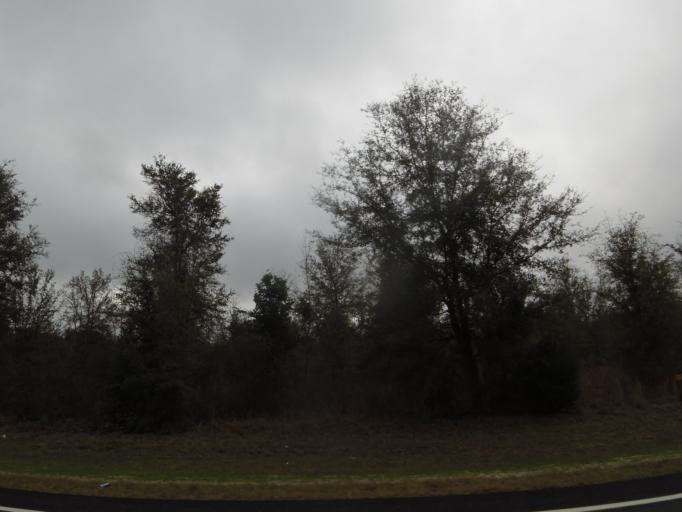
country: US
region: Florida
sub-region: Alachua County
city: High Springs
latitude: 29.8199
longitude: -82.6766
